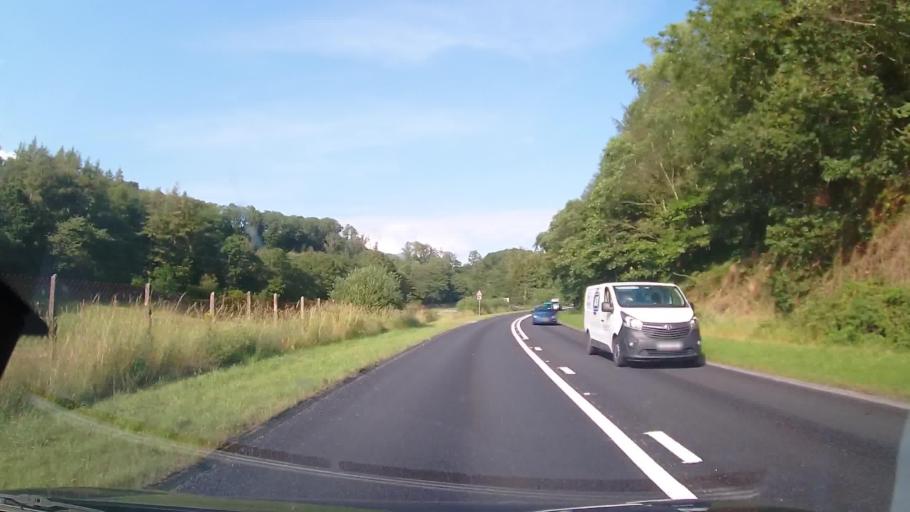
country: GB
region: Wales
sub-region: Gwynedd
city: Penrhyndeudraeth
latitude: 52.9390
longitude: -4.0500
